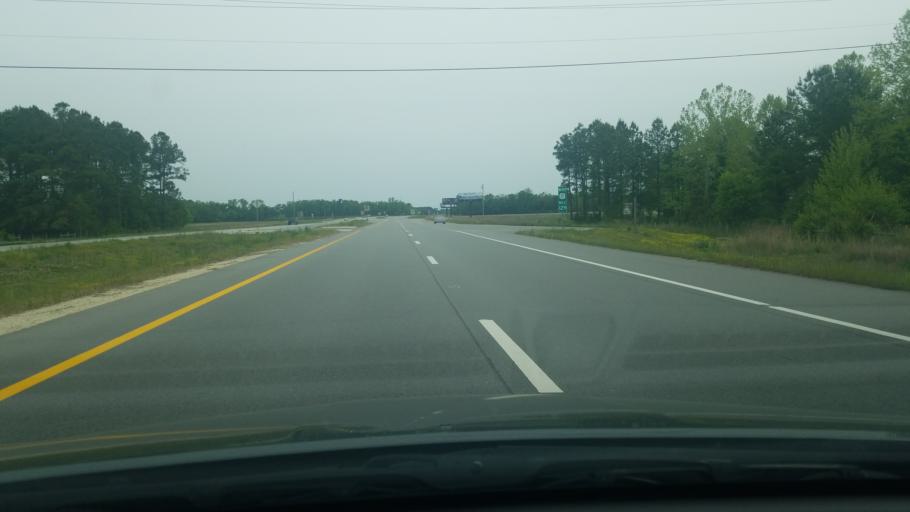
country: US
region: North Carolina
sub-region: Jones County
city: Maysville
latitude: 34.9735
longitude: -77.2396
